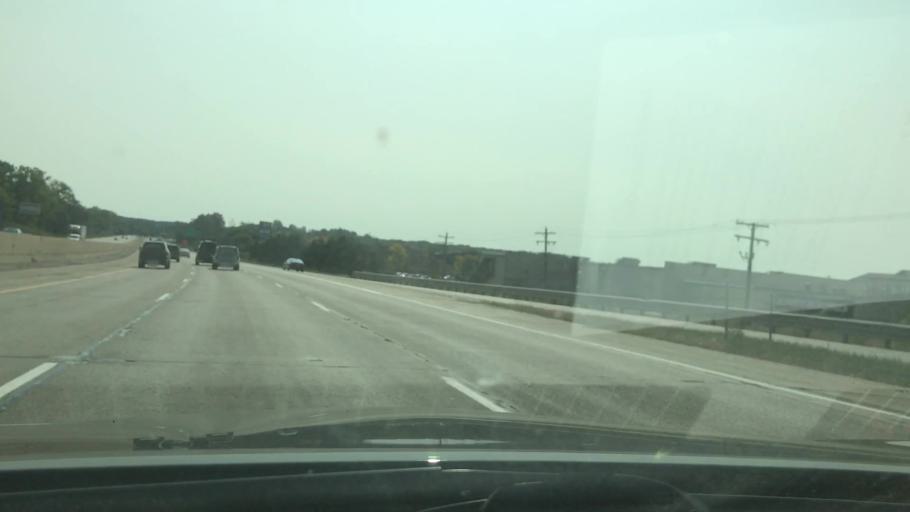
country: US
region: Michigan
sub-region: Livingston County
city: Brighton
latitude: 42.5457
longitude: -83.7861
